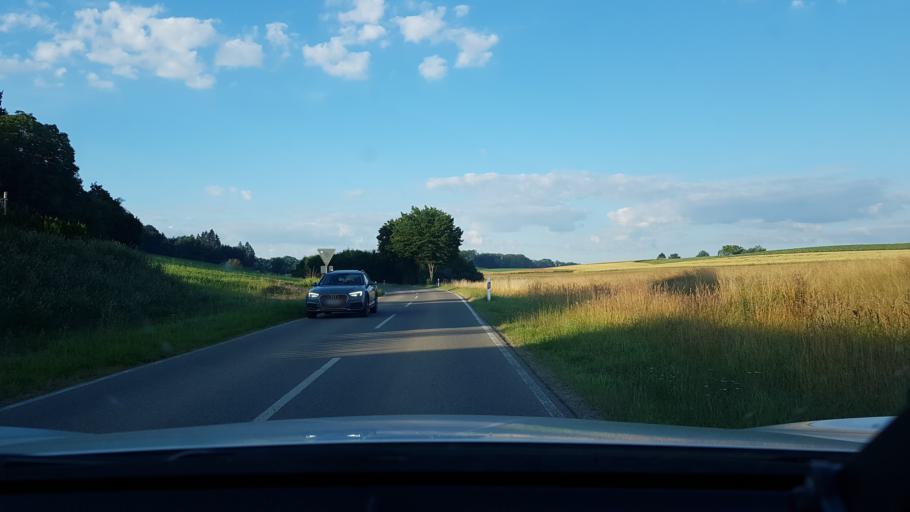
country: DE
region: Baden-Wuerttemberg
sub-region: Tuebingen Region
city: Warthausen
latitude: 48.1872
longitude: 9.8177
